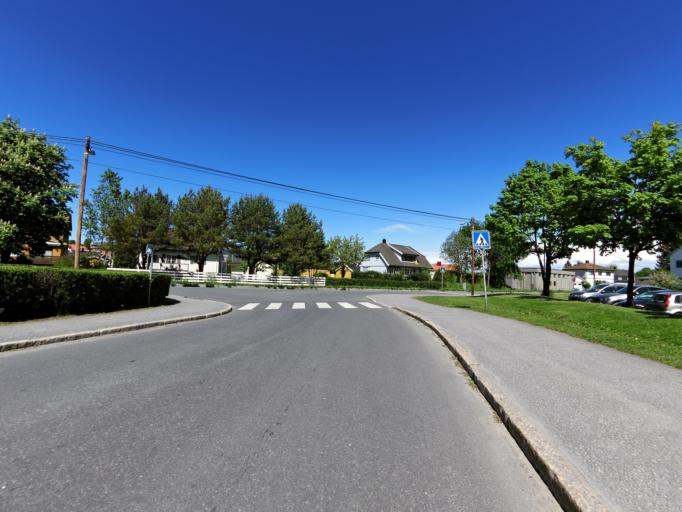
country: NO
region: Ostfold
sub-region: Fredrikstad
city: Fredrikstad
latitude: 59.2323
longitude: 10.9727
